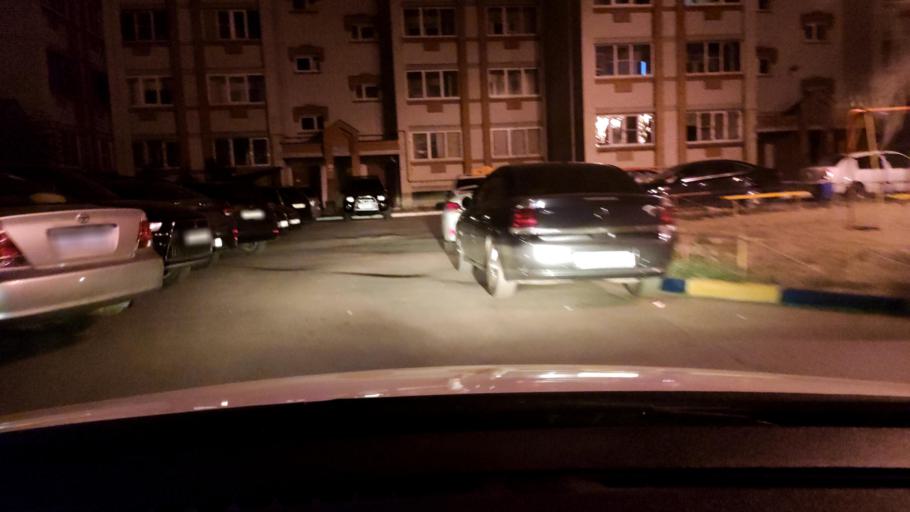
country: RU
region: Voronezj
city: Voronezh
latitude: 51.6941
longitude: 39.2075
